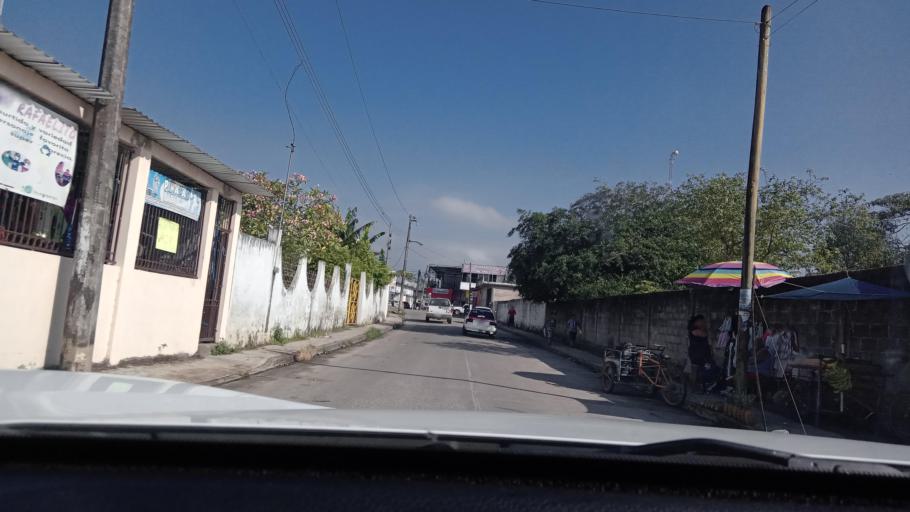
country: MX
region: Veracruz
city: Las Choapas
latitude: 17.8934
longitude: -94.1035
